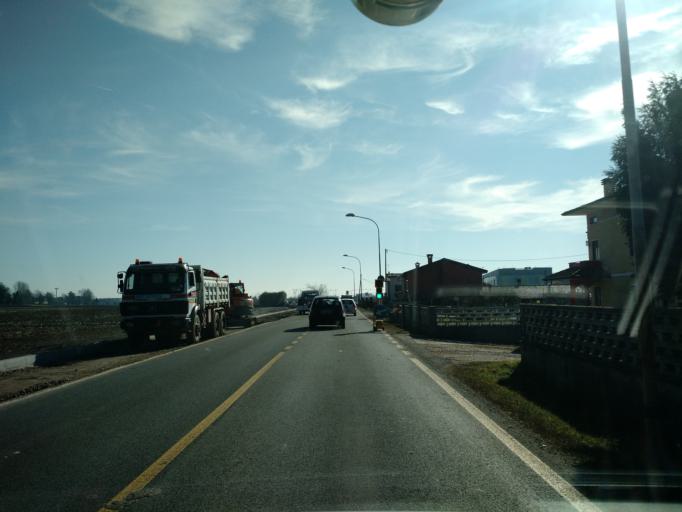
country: IT
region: Veneto
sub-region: Provincia di Vicenza
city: Santorso
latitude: 45.7308
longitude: 11.4121
